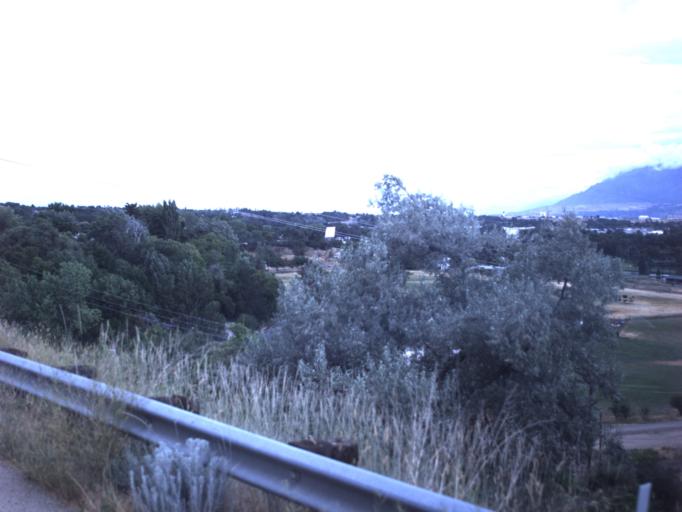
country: US
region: Utah
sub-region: Weber County
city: Riverdale
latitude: 41.1569
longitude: -112.0028
